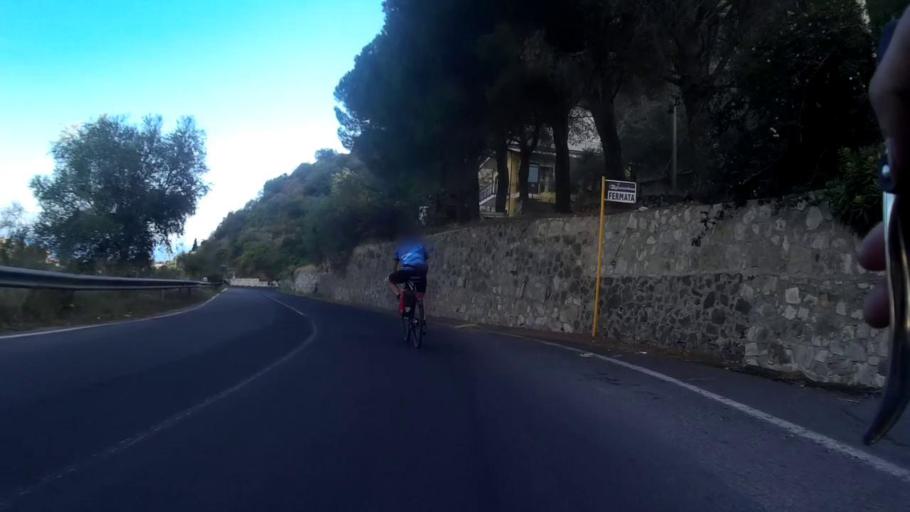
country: IT
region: Sicily
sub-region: Messina
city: Castelmola
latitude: 37.8603
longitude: 15.2800
